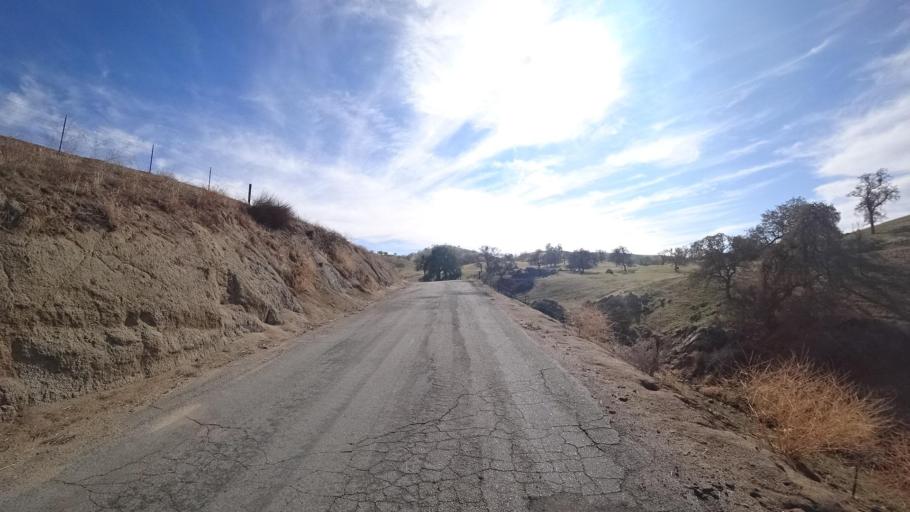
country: US
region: California
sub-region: Kern County
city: Oildale
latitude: 35.6144
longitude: -118.8422
